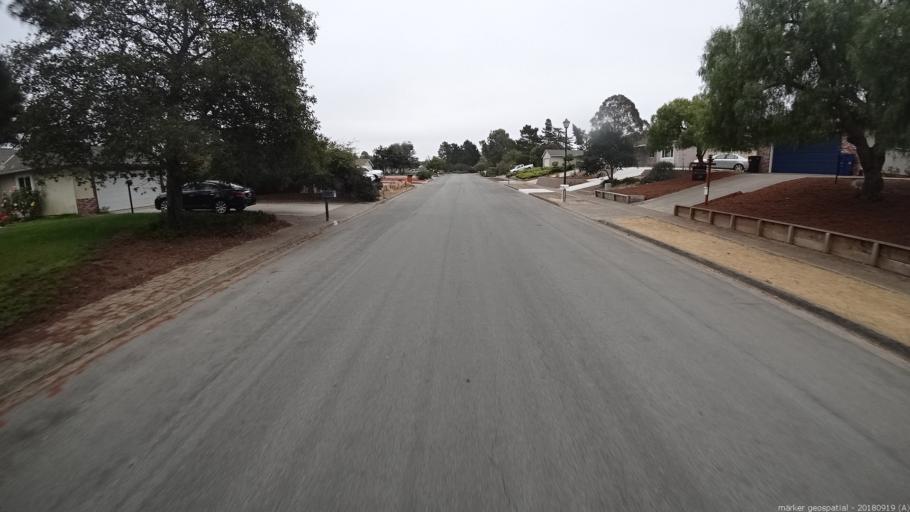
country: US
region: California
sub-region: Monterey County
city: Castroville
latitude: 36.7763
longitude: -121.7253
